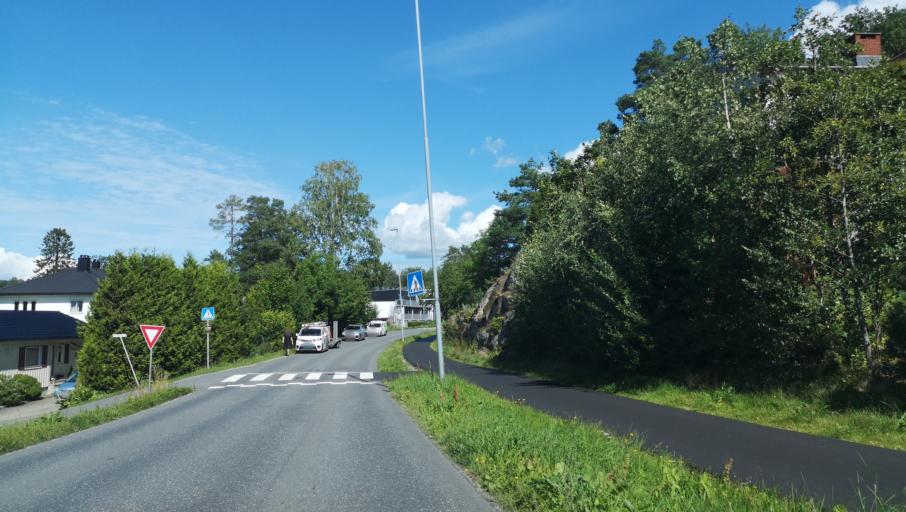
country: NO
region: Akershus
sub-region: Frogn
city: Drobak
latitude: 59.6633
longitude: 10.6403
